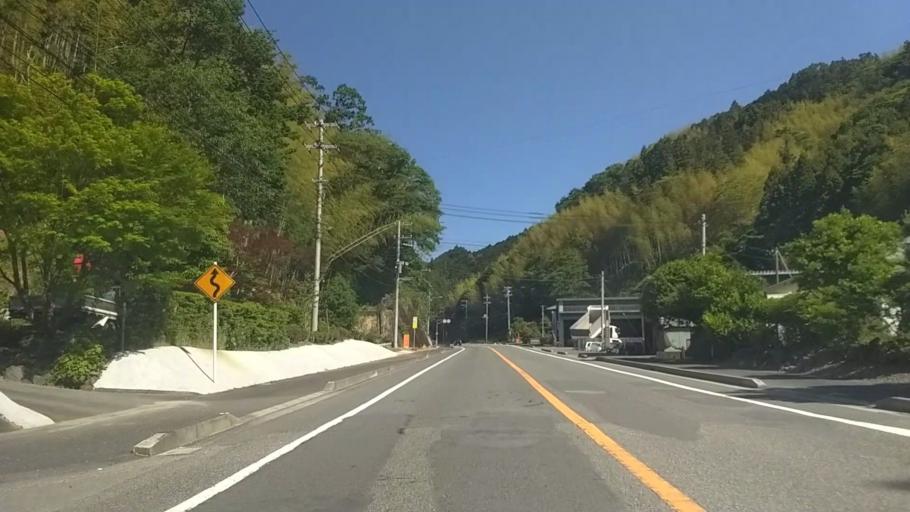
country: JP
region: Shizuoka
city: Fujinomiya
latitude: 35.2654
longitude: 138.4617
